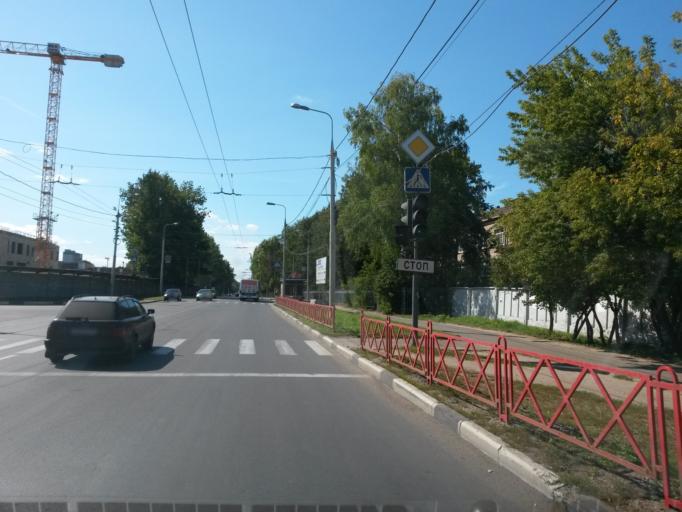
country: RU
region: Jaroslavl
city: Yaroslavl
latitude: 57.5891
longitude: 39.8463
